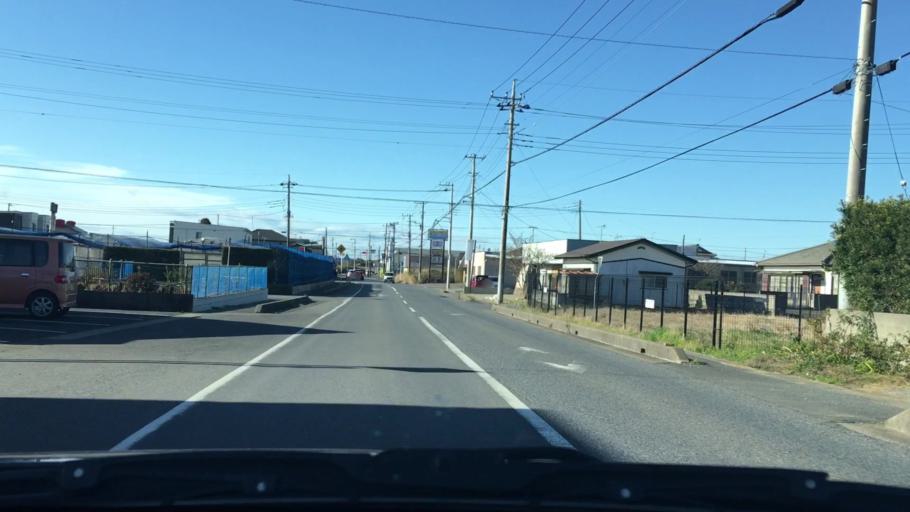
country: JP
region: Chiba
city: Omigawa
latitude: 35.8608
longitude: 140.7018
